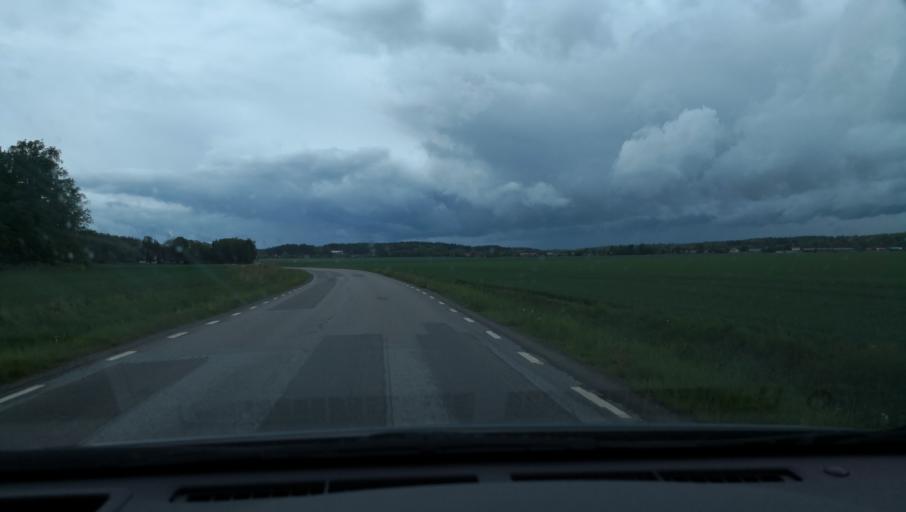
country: SE
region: Uppsala
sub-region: Enkopings Kommun
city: Orsundsbro
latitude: 59.7225
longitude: 17.3301
